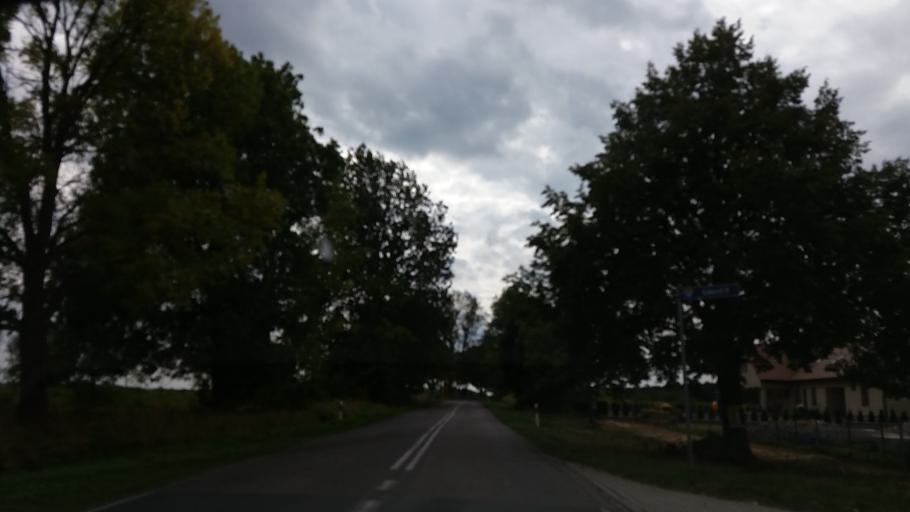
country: PL
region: West Pomeranian Voivodeship
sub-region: Powiat stargardzki
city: Kobylanka
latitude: 53.3359
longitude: 14.8621
